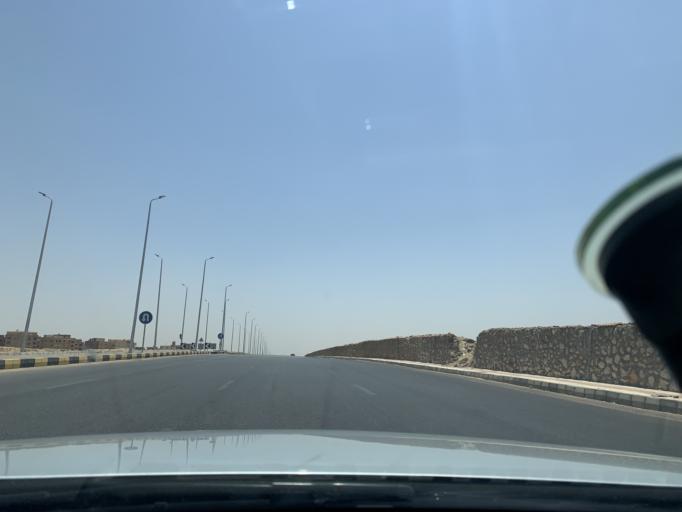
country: EG
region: Muhafazat al Qahirah
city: Halwan
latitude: 29.9891
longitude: 31.4686
